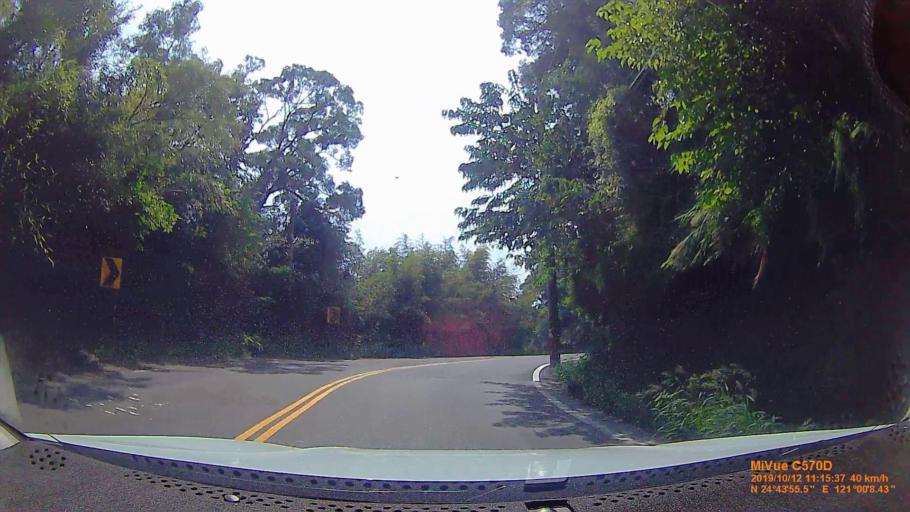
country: TW
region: Taiwan
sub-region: Hsinchu
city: Hsinchu
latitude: 24.7322
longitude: 121.0023
